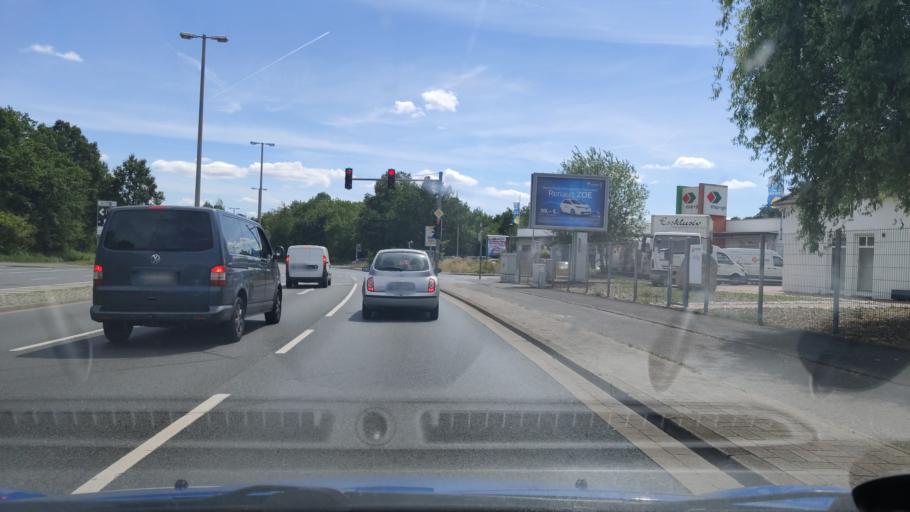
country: DE
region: Lower Saxony
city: Ronnenberg
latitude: 52.3499
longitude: 9.6896
